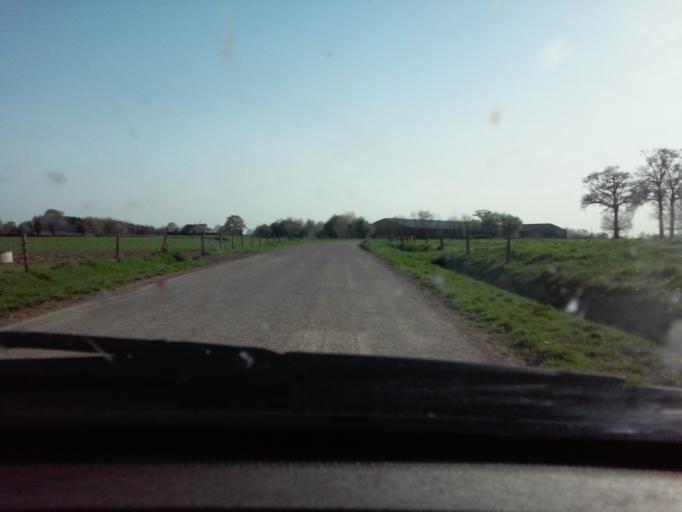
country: FR
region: Brittany
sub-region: Departement d'Ille-et-Vilaine
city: Romagne
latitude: 48.3045
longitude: -1.2645
